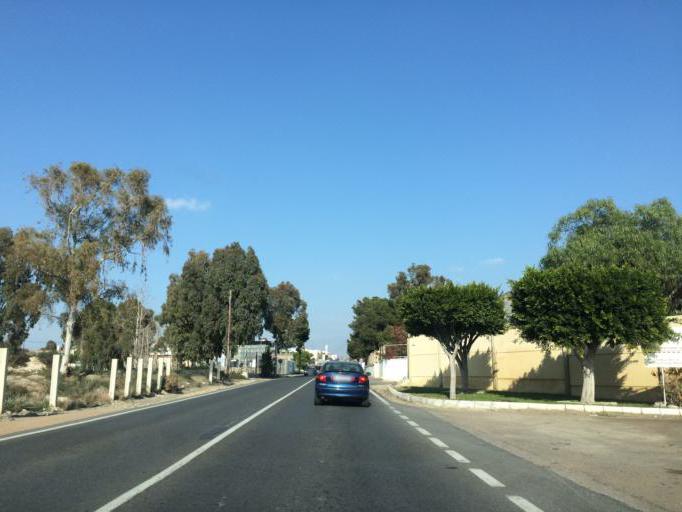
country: ES
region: Andalusia
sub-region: Provincia de Almeria
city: Huercal de Almeria
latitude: 36.8521
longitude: -2.4206
